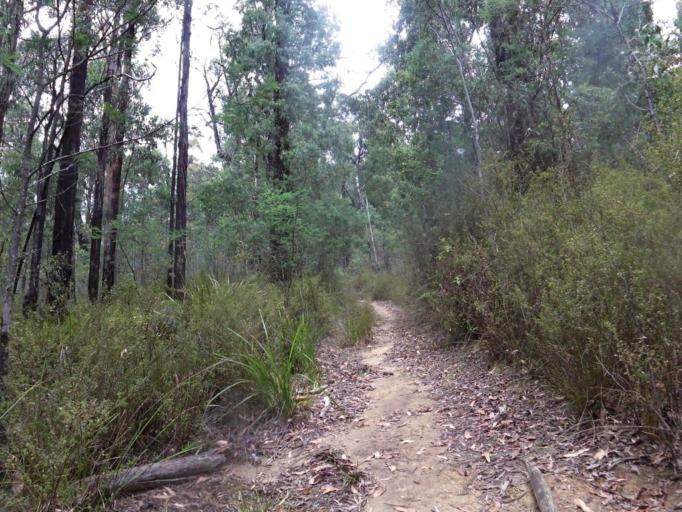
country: AU
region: Victoria
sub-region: Yarra Ranges
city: Healesville
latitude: -37.4520
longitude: 145.5839
